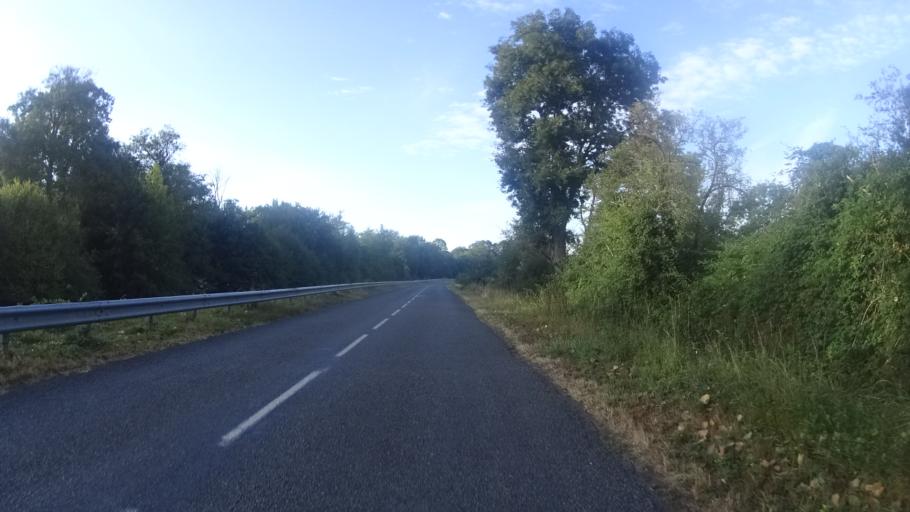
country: FR
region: Bourgogne
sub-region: Departement de Saone-et-Loire
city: Paray-le-Monial
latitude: 46.4556
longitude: 4.1575
